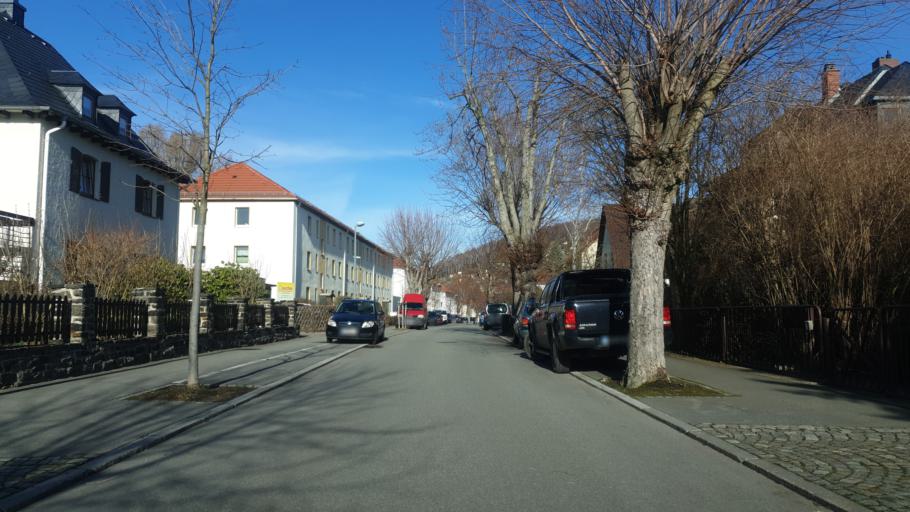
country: DE
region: Saxony
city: Aue
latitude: 50.5921
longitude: 12.7084
